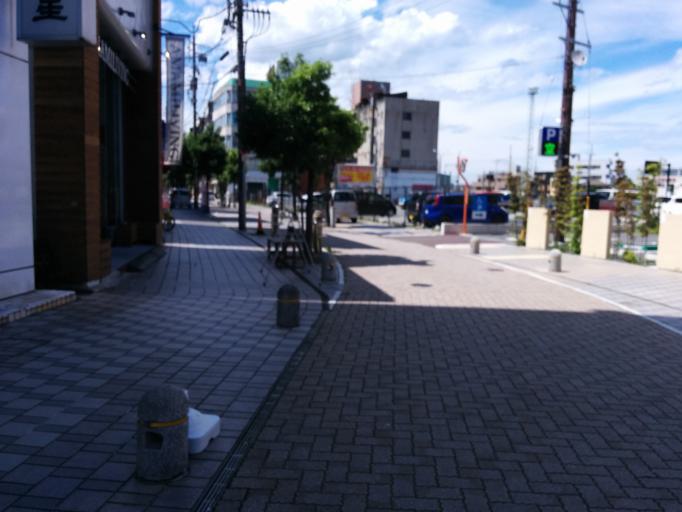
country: JP
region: Mie
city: Ise
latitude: 34.4913
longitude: 136.7083
